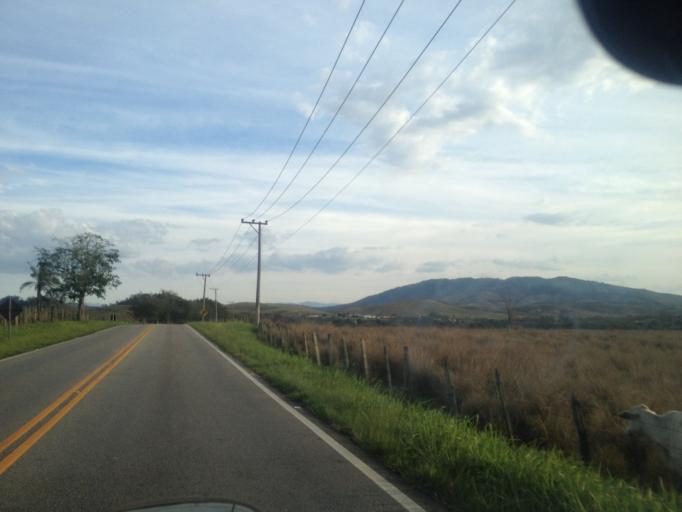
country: BR
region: Rio de Janeiro
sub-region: Porto Real
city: Porto Real
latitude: -22.4412
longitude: -44.2926
